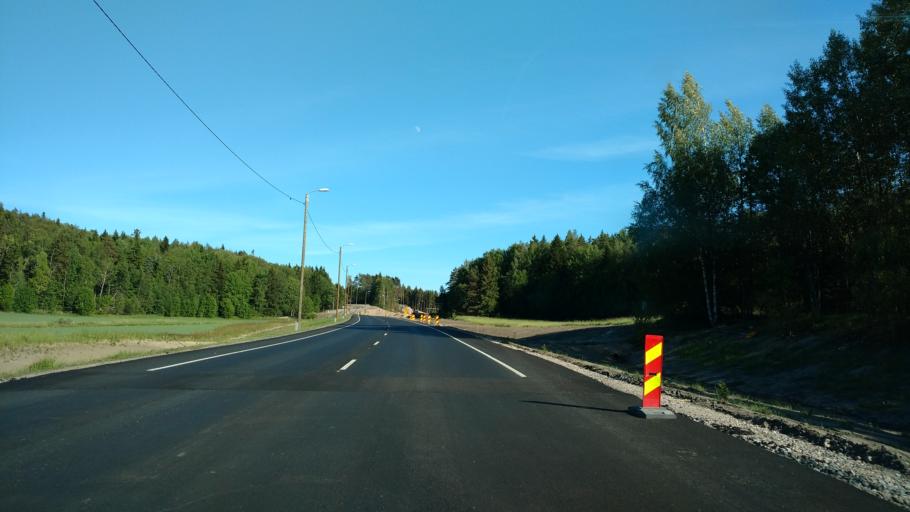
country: FI
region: Varsinais-Suomi
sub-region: Salo
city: Salo
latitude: 60.3852
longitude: 23.1690
